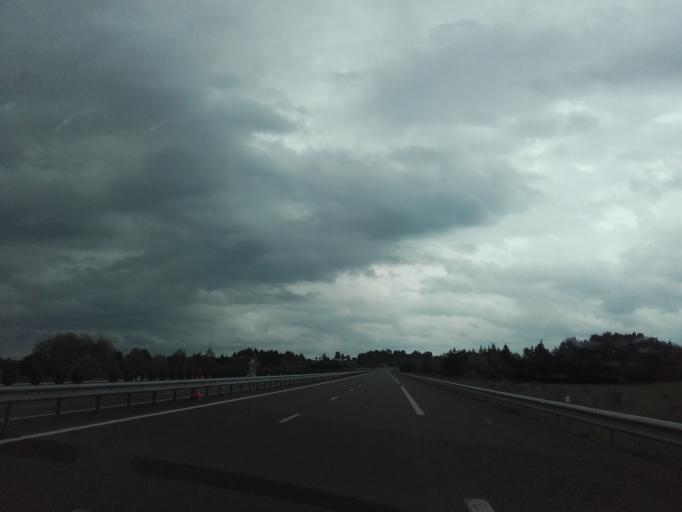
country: FR
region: Auvergne
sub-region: Departement du Puy-de-Dome
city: Saint-Sauves-d'Auvergne
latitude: 45.6262
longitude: 2.4961
